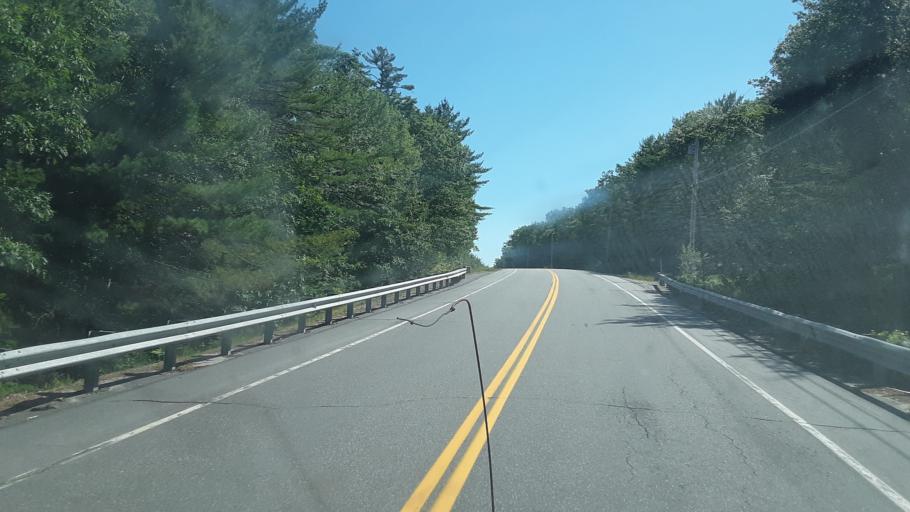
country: US
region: Maine
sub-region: Hancock County
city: Franklin
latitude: 44.6096
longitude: -68.2022
